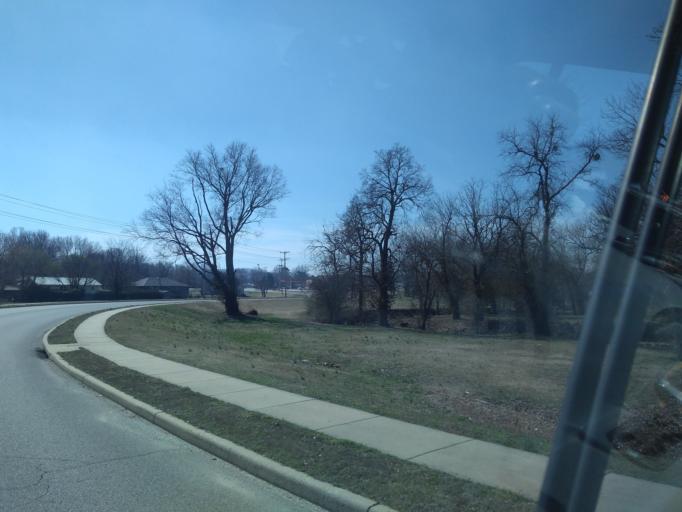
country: US
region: Arkansas
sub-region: Washington County
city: Farmington
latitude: 36.0461
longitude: -94.2356
